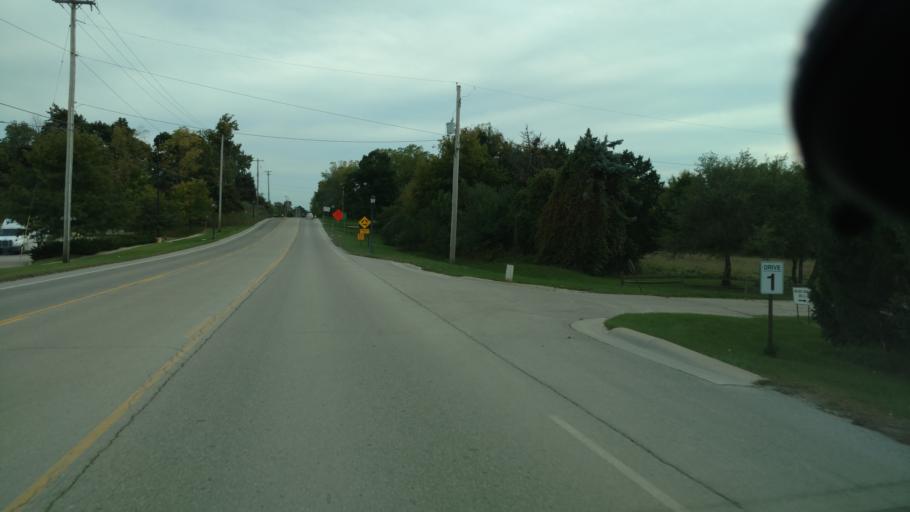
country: US
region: Michigan
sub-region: Ingham County
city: Lansing
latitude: 42.7657
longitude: -84.5231
